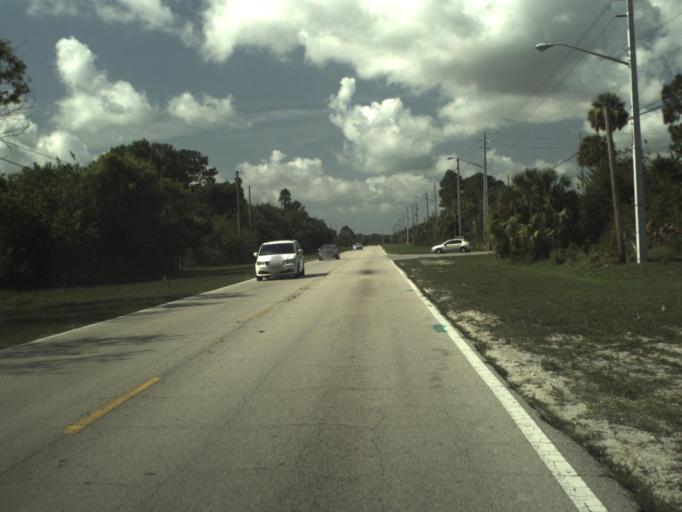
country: US
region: Florida
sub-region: Saint Lucie County
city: Port Saint Lucie
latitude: 27.2402
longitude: -80.3769
